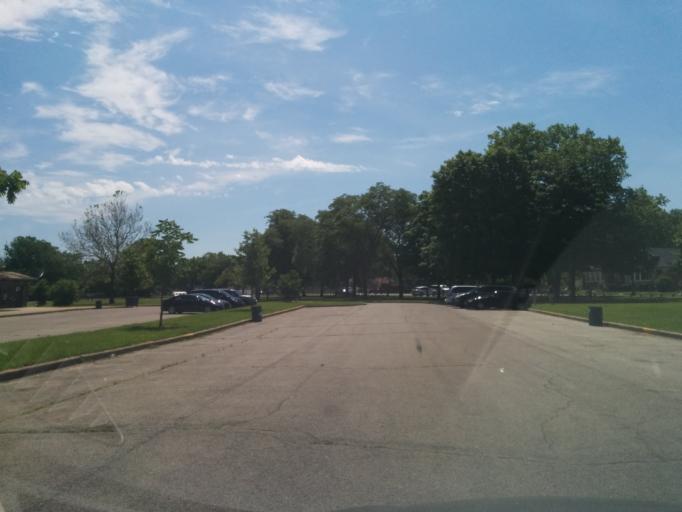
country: US
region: Illinois
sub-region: Cook County
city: Lincolnwood
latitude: 41.9761
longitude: -87.7417
